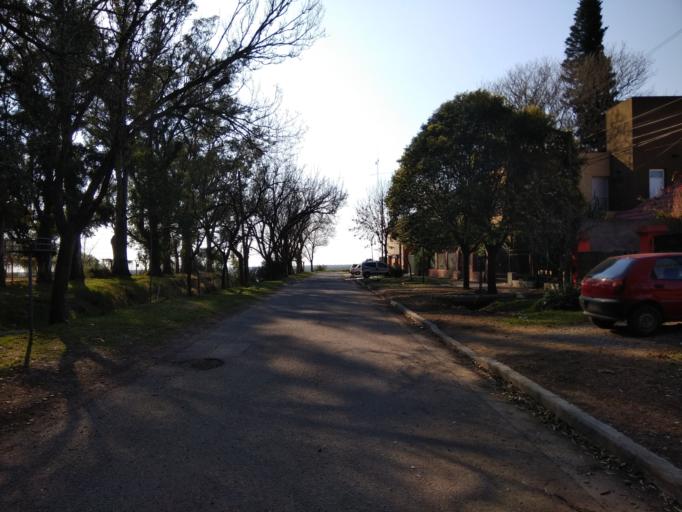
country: AR
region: Santa Fe
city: Granadero Baigorria
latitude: -32.8473
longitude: -60.6982
